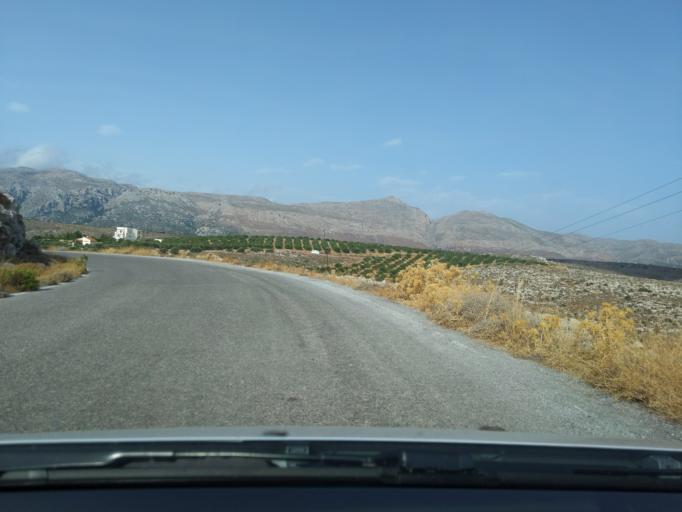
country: GR
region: Crete
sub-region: Nomos Lasithiou
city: Palekastro
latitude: 35.0863
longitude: 26.2487
